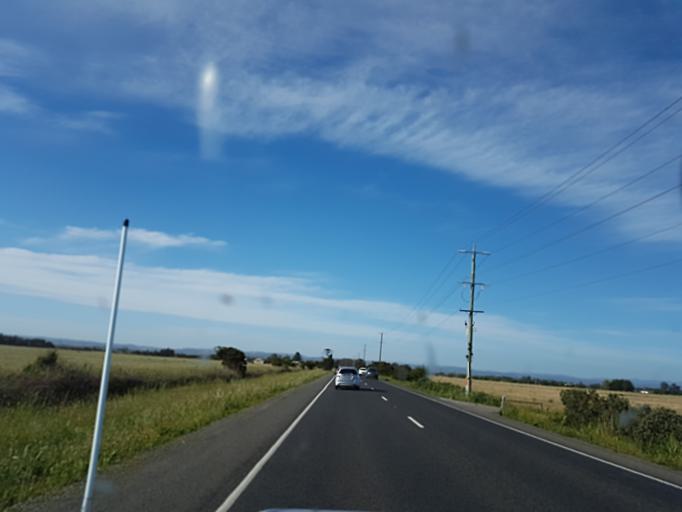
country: AU
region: Victoria
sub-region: Cardinia
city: Pakenham South
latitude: -38.1454
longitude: 145.4874
